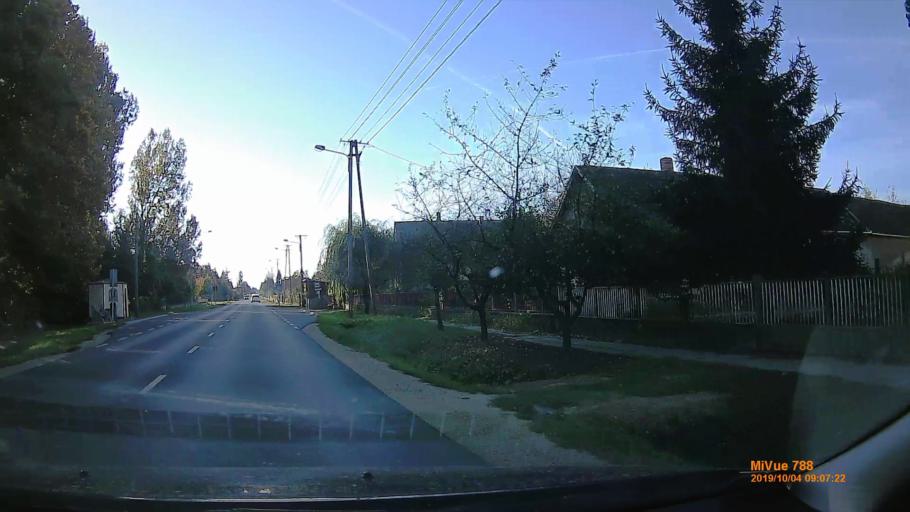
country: HU
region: Somogy
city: Karad
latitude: 46.6789
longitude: 17.7737
